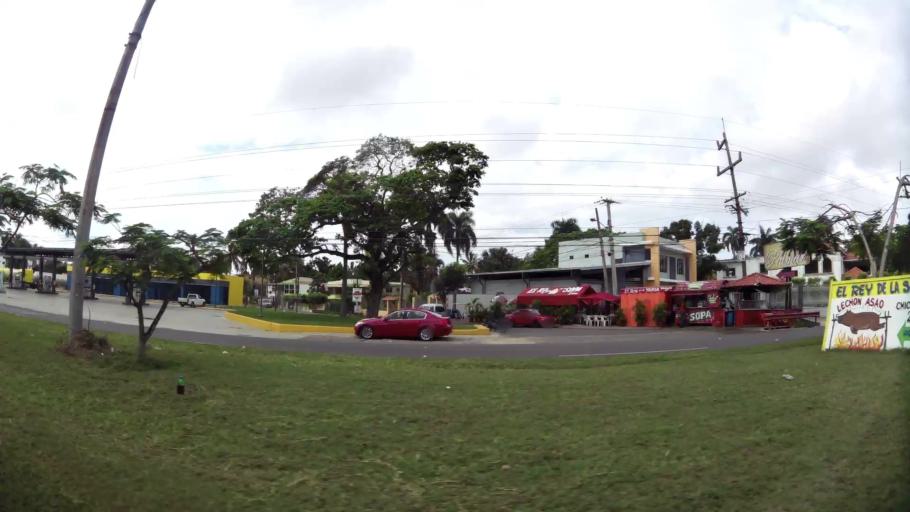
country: DO
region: Santiago
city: Licey al Medio
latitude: 19.4227
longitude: -70.6499
